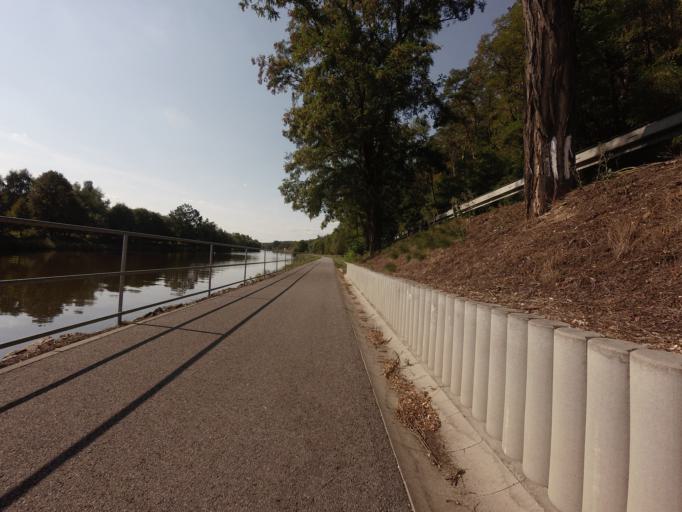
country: CZ
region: Jihocesky
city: Tyn nad Vltavou
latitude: 49.2126
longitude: 14.4404
